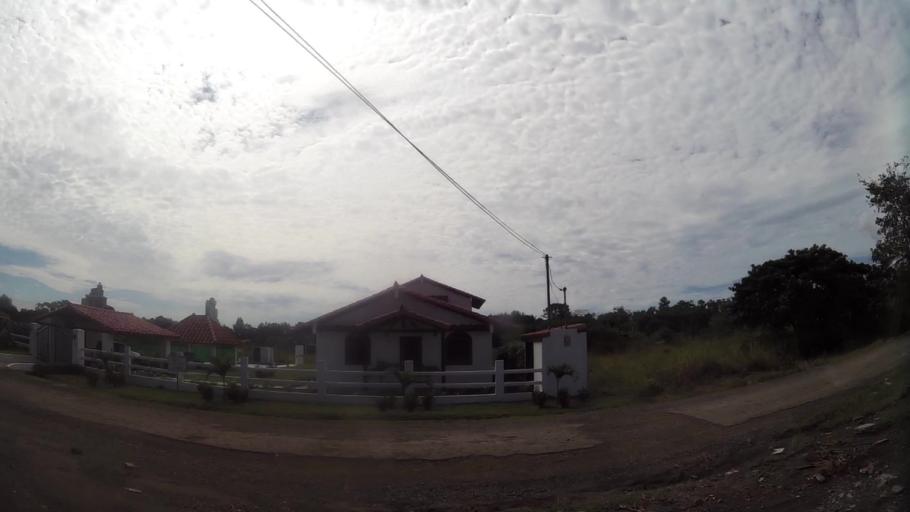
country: PA
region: Panama
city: Nueva Gorgona
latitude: 8.5462
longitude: -79.8921
